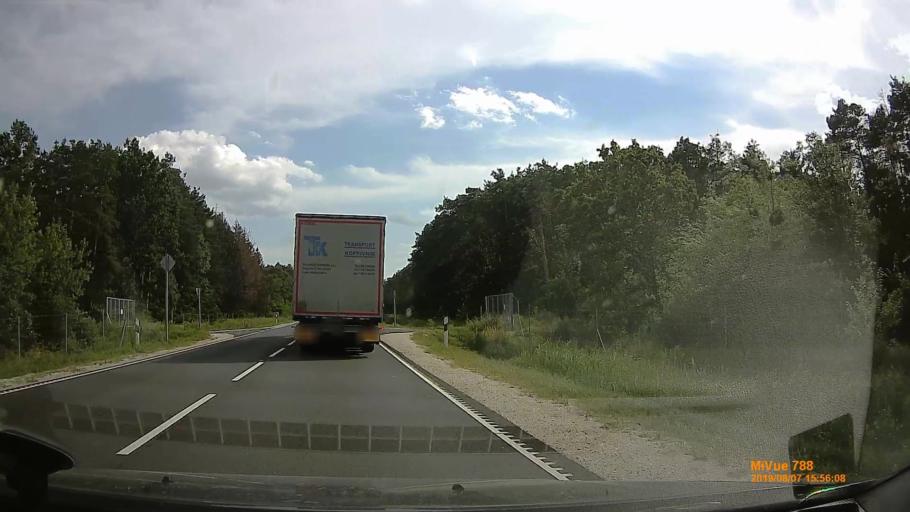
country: HU
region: Vas
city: Kormend
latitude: 47.0650
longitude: 16.6165
